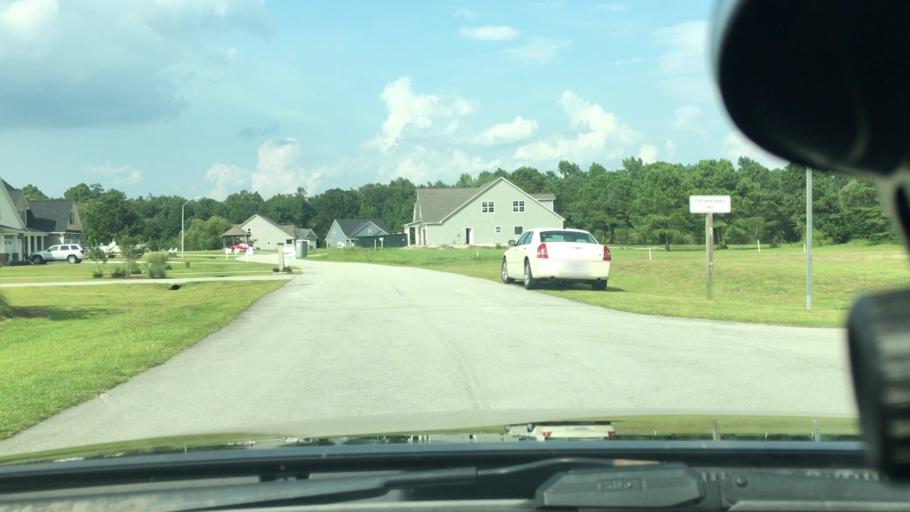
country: US
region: North Carolina
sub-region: Craven County
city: New Bern
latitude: 35.1841
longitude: -77.0539
